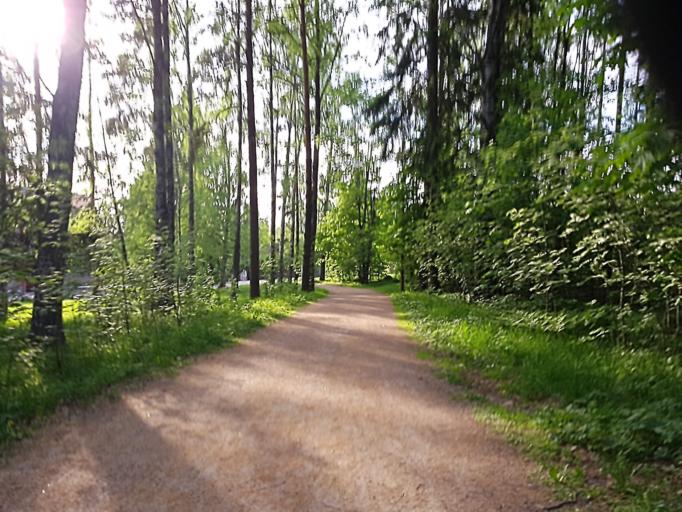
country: FI
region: Uusimaa
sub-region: Helsinki
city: Helsinki
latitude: 60.2437
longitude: 24.9379
